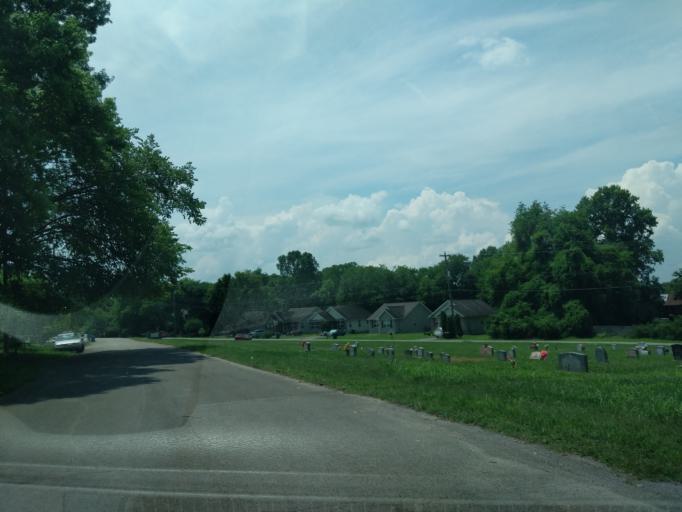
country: US
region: Tennessee
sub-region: Davidson County
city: Lakewood
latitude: 36.2296
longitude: -86.6346
